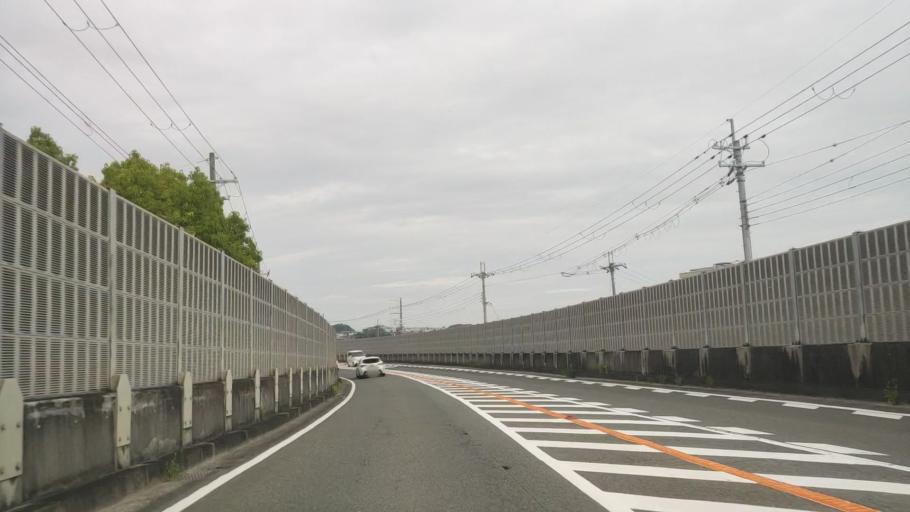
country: JP
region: Osaka
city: Tondabayashicho
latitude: 34.4295
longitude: 135.5694
